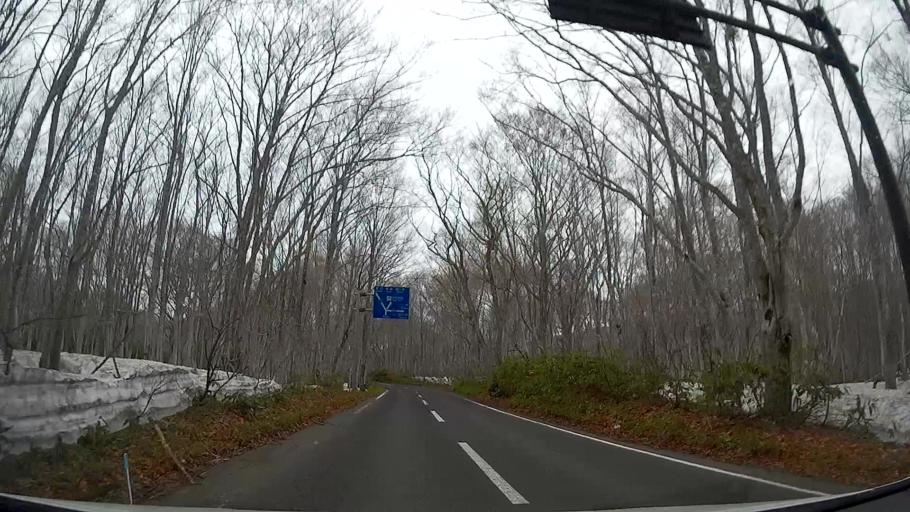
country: JP
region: Aomori
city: Aomori Shi
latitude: 40.6311
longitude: 140.9318
